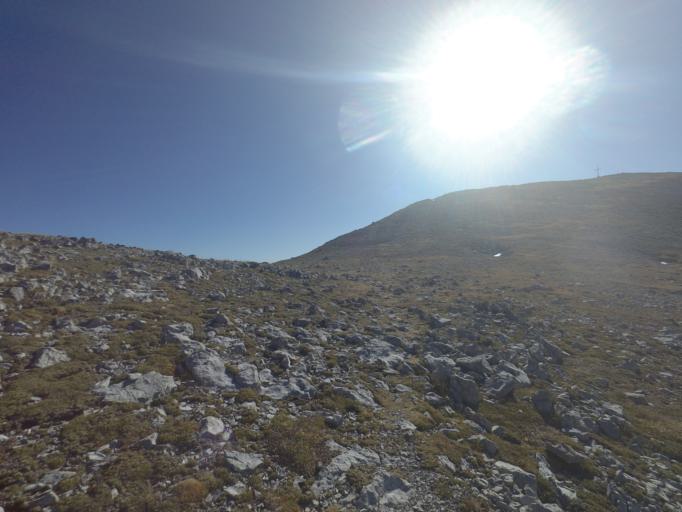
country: AT
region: Salzburg
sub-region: Politischer Bezirk Sankt Johann im Pongau
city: Werfenweng
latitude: 47.5004
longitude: 13.2266
